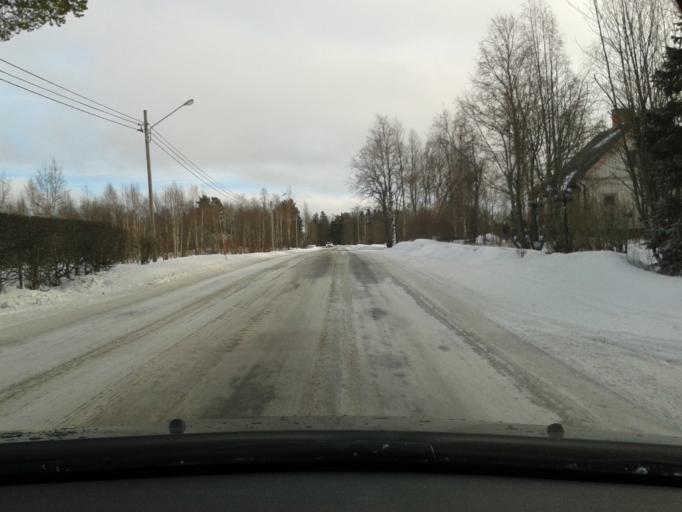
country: SE
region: Vaesterbotten
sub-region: Vilhelmina Kommun
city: Sjoberg
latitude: 64.6326
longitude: 16.4012
